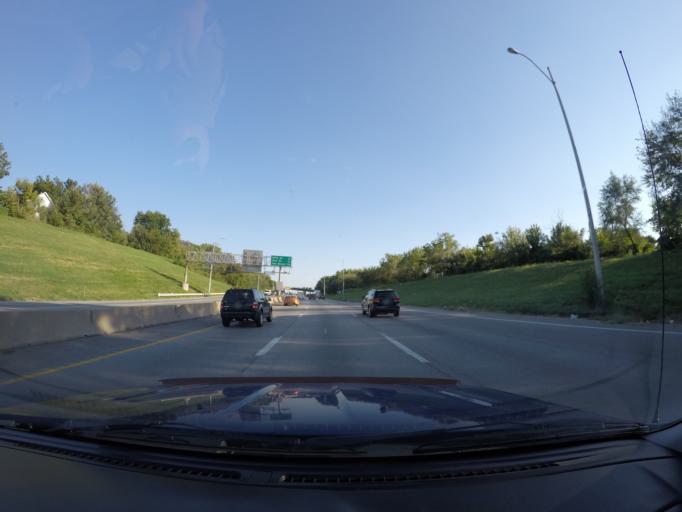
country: US
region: Missouri
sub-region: Jackson County
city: Kansas City
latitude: 39.0822
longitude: -94.5411
